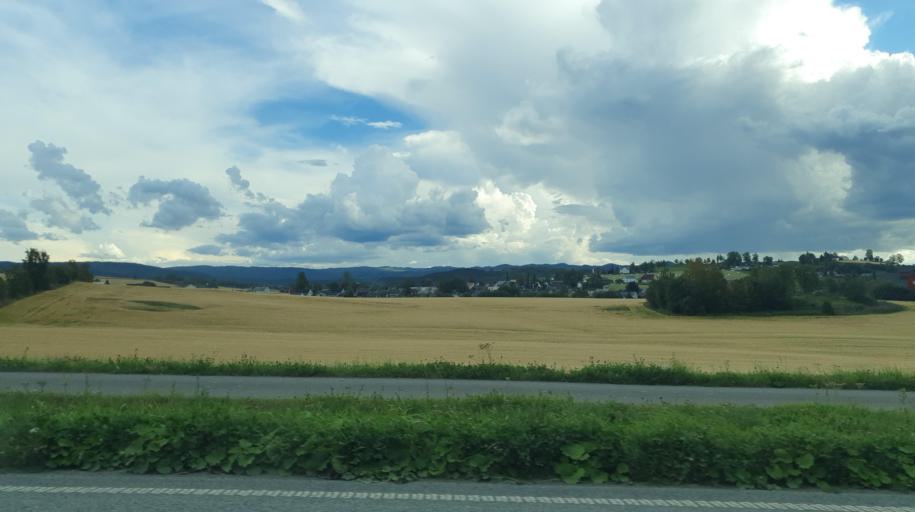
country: NO
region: Nord-Trondelag
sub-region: Levanger
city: Levanger
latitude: 63.7510
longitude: 11.3268
